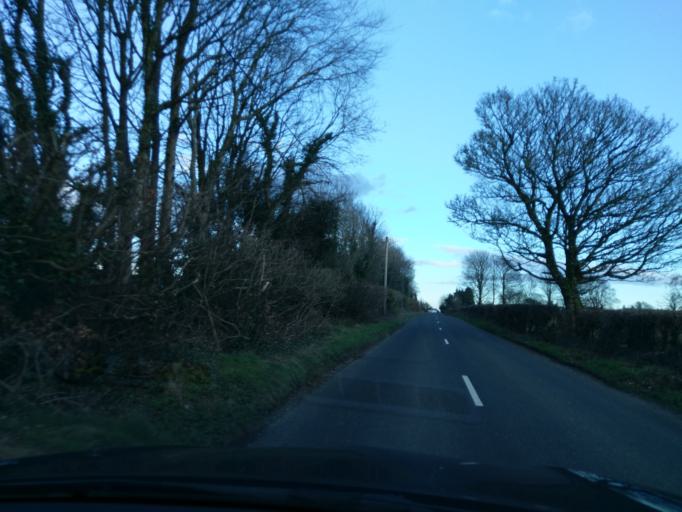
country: IE
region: Connaught
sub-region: County Galway
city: Athenry
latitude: 53.4300
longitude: -8.6999
